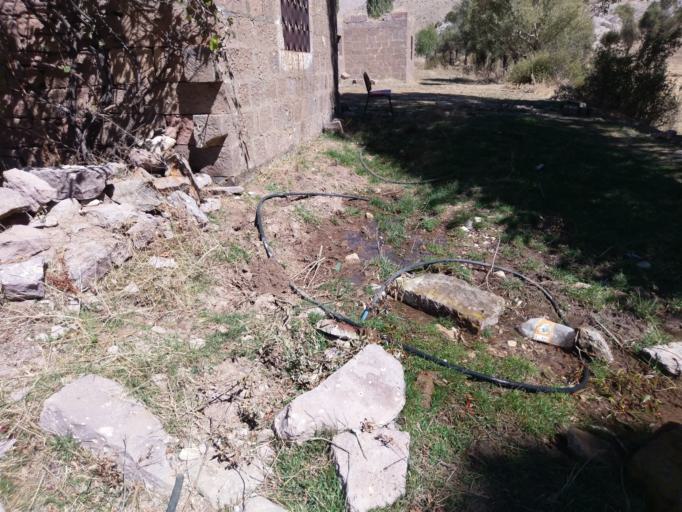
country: TR
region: Kayseri
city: Toklar
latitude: 38.4051
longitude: 36.1254
